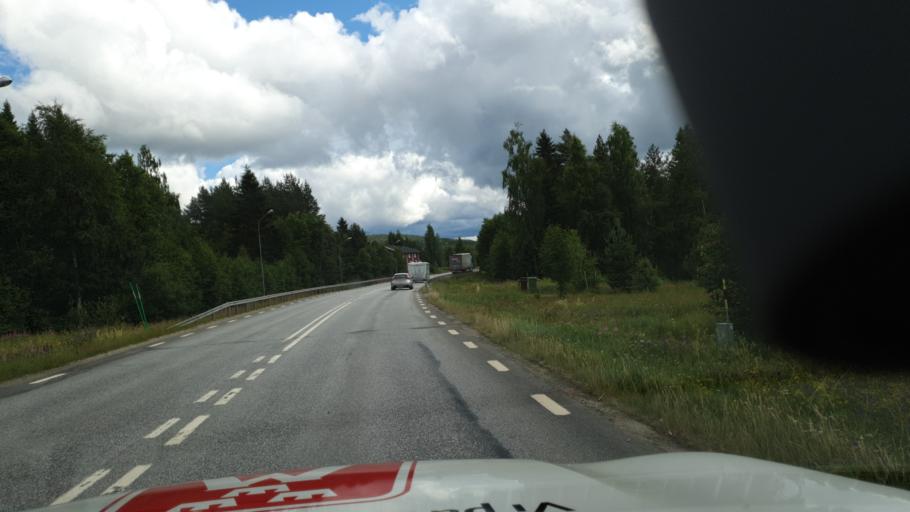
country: SE
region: Vaesterbotten
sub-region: Vannas Kommun
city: Vaennaes
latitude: 63.9650
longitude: 19.7490
